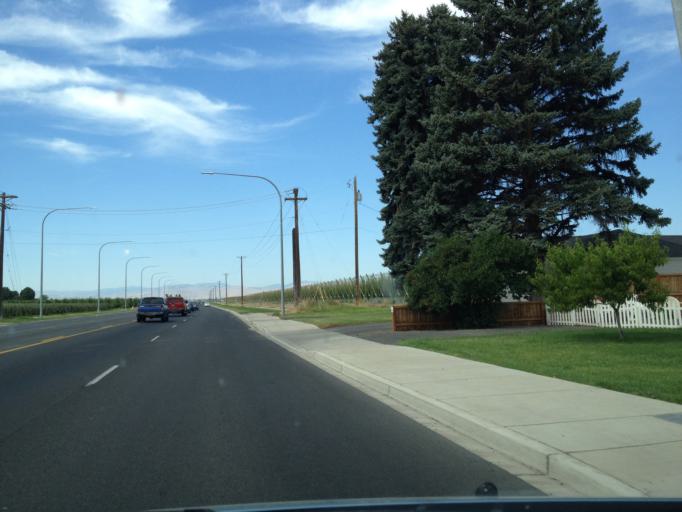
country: US
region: Washington
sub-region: Yakima County
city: West Valley
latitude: 46.5855
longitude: -120.5794
